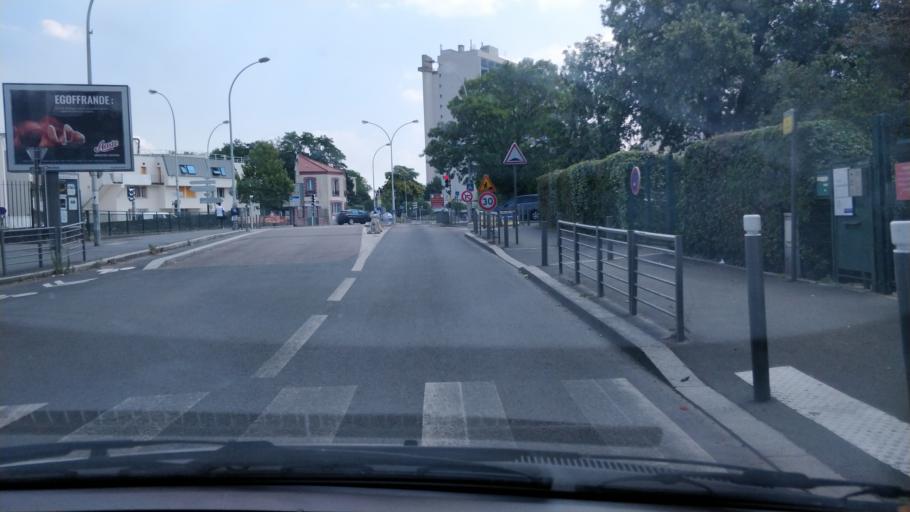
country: FR
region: Ile-de-France
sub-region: Departement de Seine-Saint-Denis
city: Les Lilas
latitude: 48.8738
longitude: 2.4276
